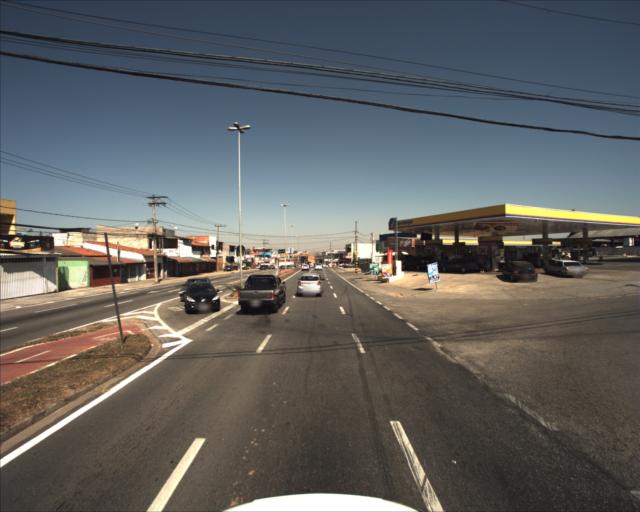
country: BR
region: Sao Paulo
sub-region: Sorocaba
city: Sorocaba
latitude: -23.4394
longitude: -47.4778
